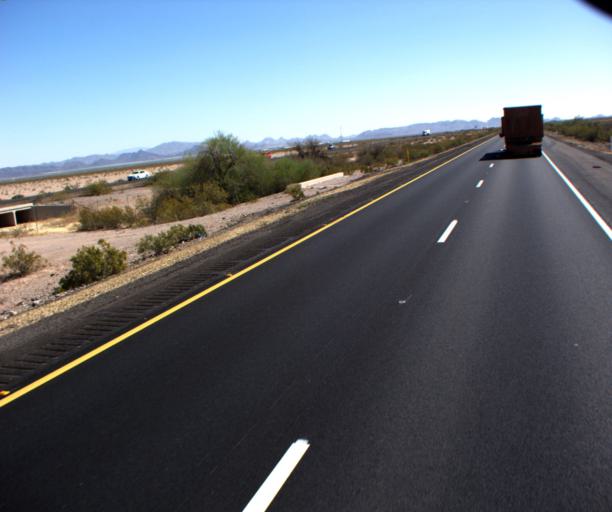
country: US
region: Arizona
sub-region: La Paz County
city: Salome
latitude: 33.6365
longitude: -113.8069
